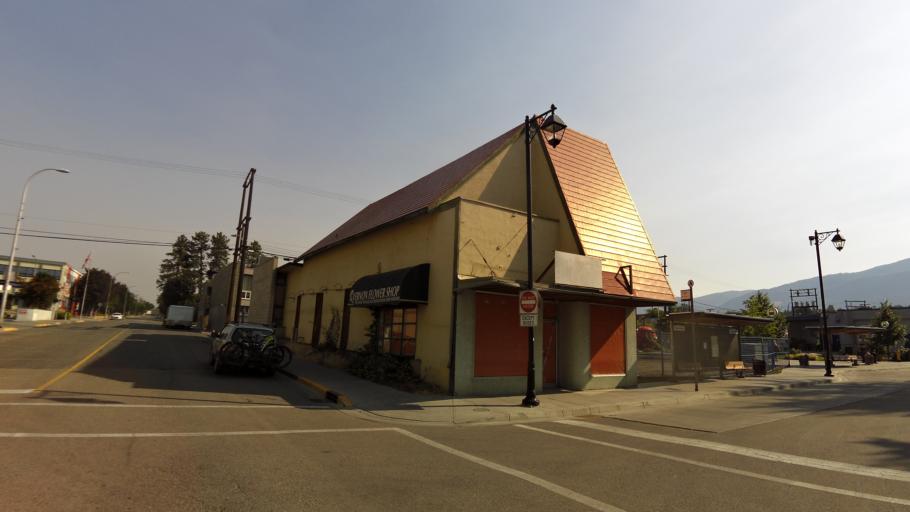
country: CA
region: British Columbia
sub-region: Regional District of North Okanagan
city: Vernon
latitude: 50.2645
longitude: -119.2723
